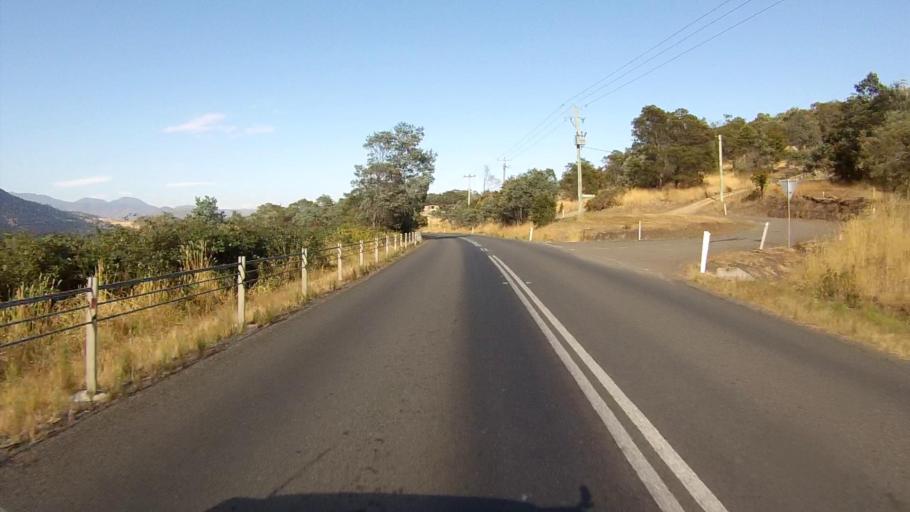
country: AU
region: Tasmania
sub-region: Glenorchy
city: Granton
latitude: -42.7550
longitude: 147.1444
